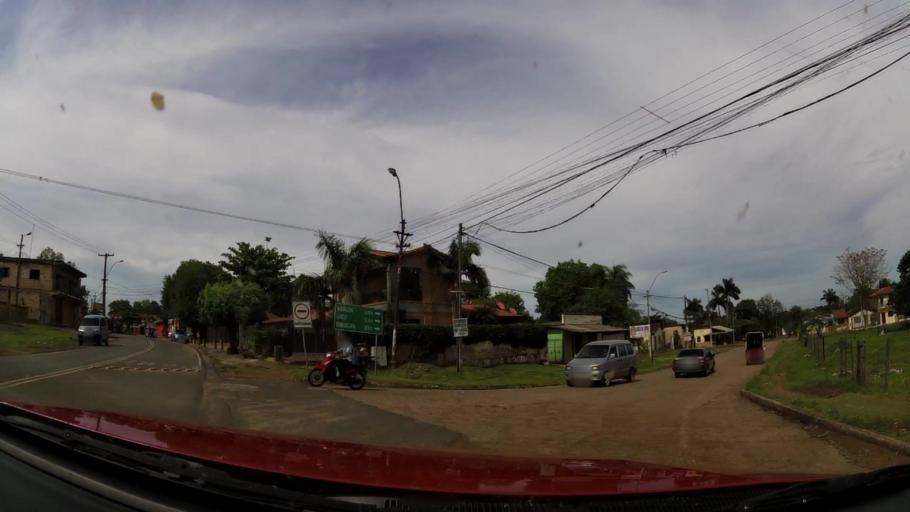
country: PY
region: Central
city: Limpio
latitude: -25.1622
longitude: -57.4757
